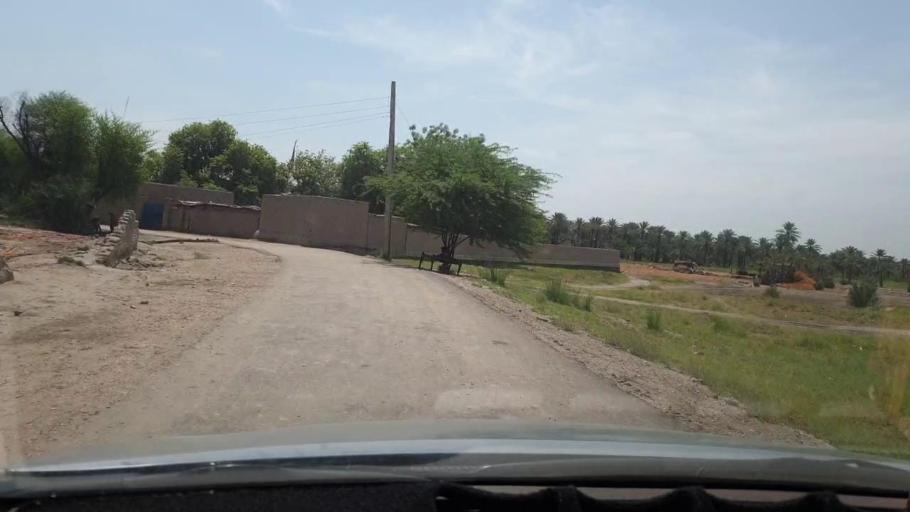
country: PK
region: Sindh
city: Khairpur
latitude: 27.4860
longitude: 68.7645
